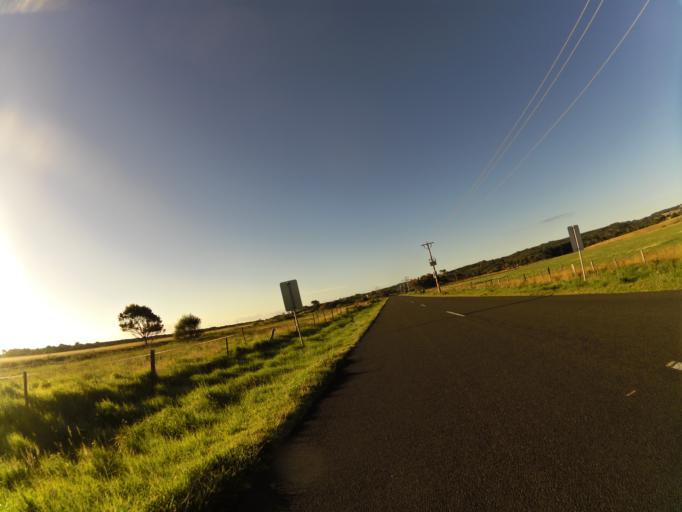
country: AU
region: Victoria
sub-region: Colac-Otway
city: Apollo Bay
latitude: -38.7630
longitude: 143.6617
